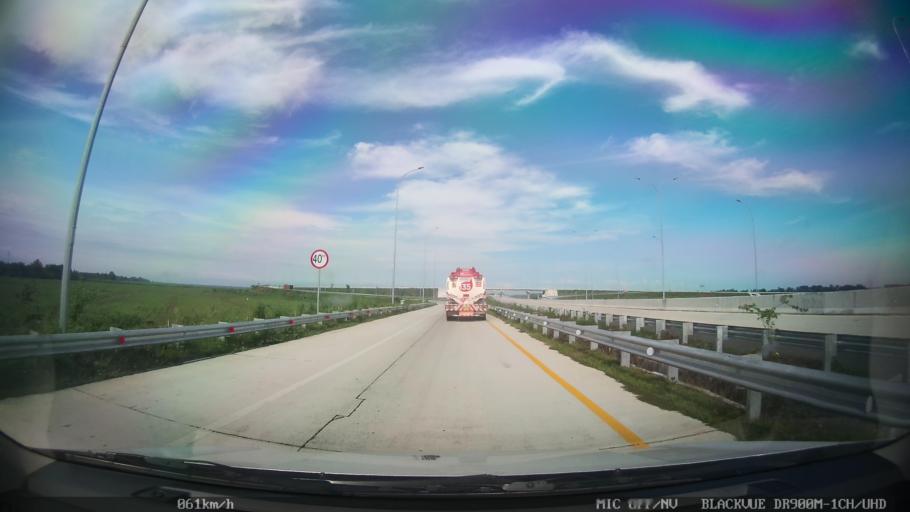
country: ID
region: North Sumatra
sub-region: Kabupaten Langkat
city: Stabat
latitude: 3.7131
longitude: 98.4980
